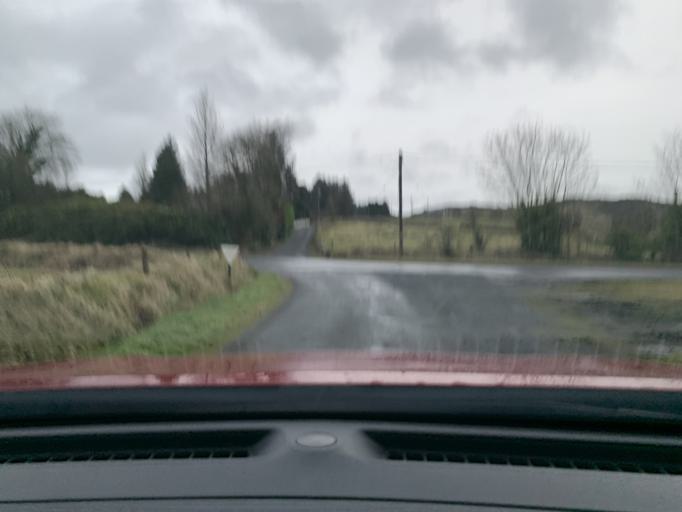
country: IE
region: Connaught
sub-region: Roscommon
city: Boyle
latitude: 53.9978
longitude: -8.3087
